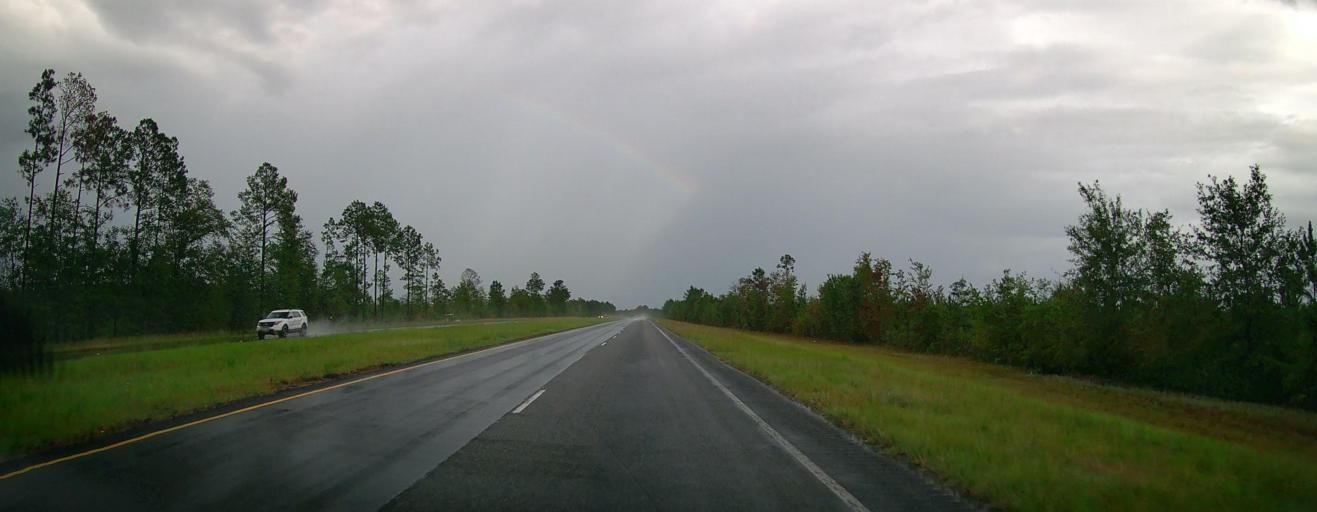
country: US
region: Georgia
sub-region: Ware County
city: Deenwood
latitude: 31.2549
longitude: -82.4602
